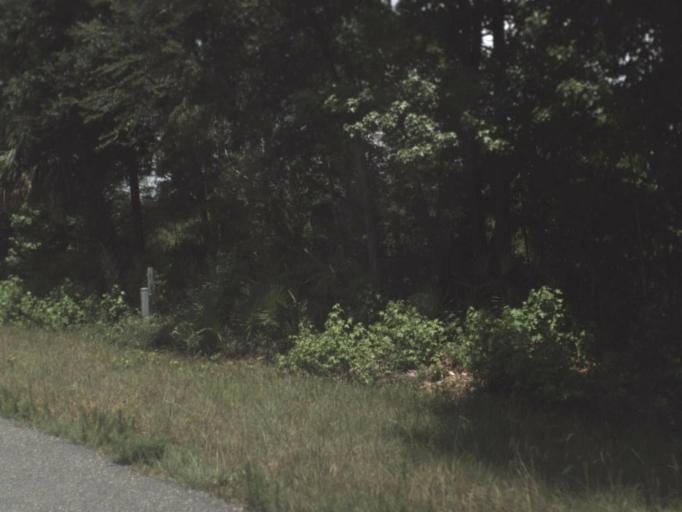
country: US
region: Florida
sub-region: Taylor County
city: Perry
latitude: 30.1411
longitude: -83.8887
